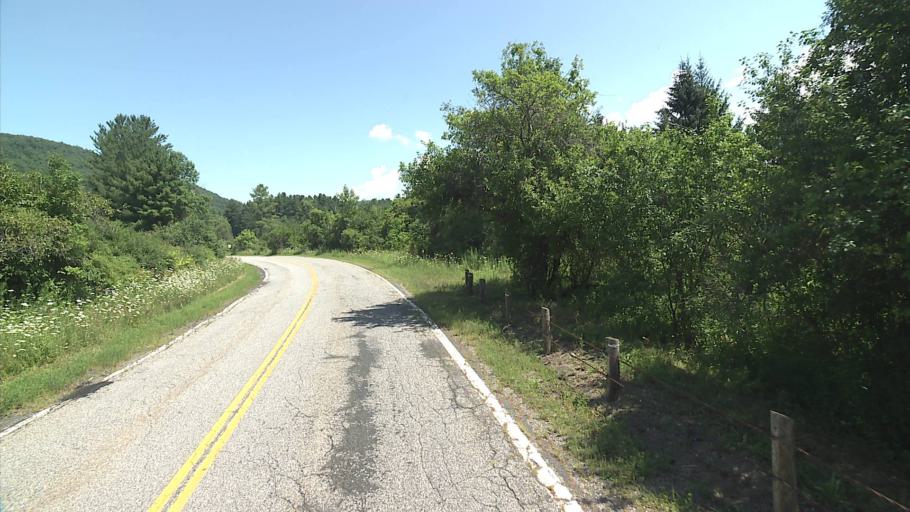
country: US
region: Connecticut
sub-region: Litchfield County
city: Canaan
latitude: 41.9017
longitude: -73.2808
